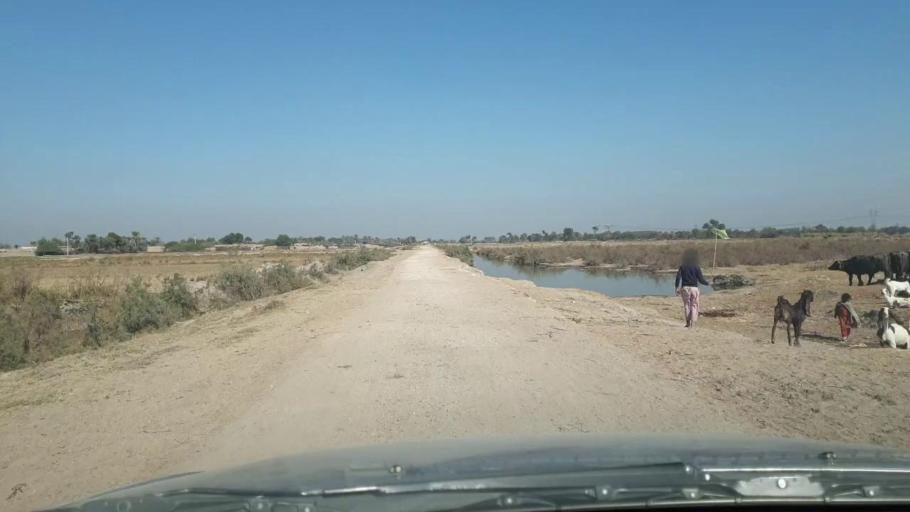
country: PK
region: Sindh
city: Adilpur
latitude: 27.8819
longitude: 69.2715
